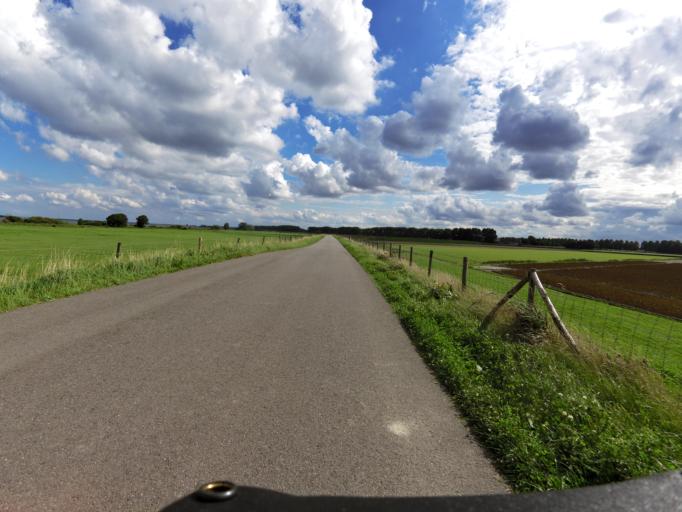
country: NL
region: South Holland
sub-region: Gemeente Goeree-Overflakkee
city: Middelharnis
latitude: 51.7329
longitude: 4.2525
